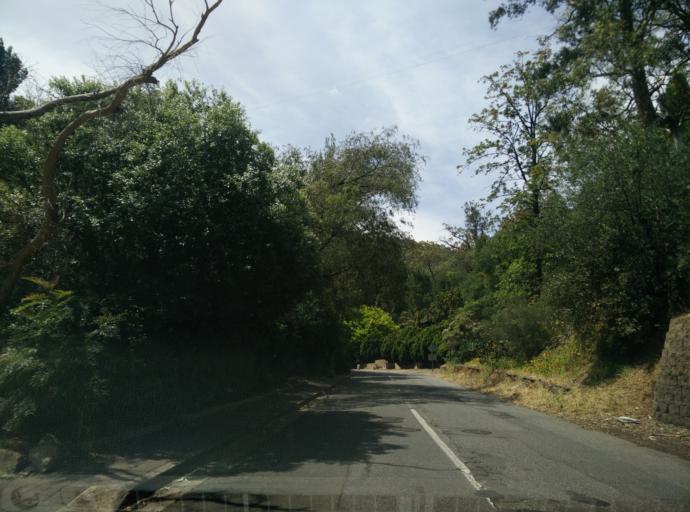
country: AU
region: South Australia
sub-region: Burnside
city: Beaumont
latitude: -34.9540
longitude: 138.6725
